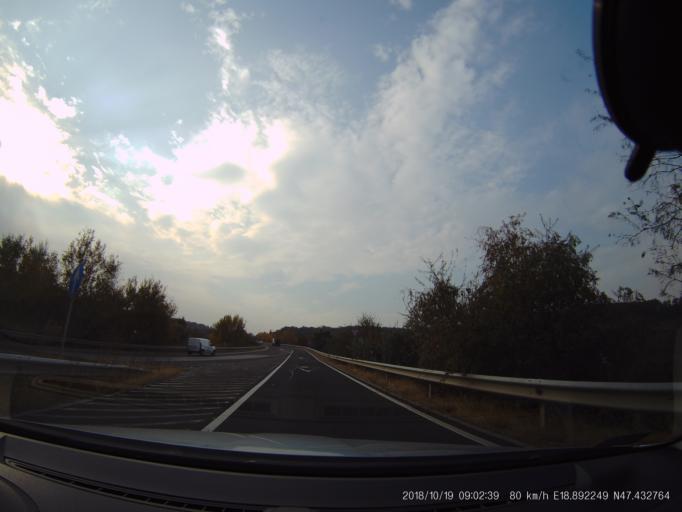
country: HU
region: Pest
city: Toeroekbalint
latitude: 47.4327
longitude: 18.8922
